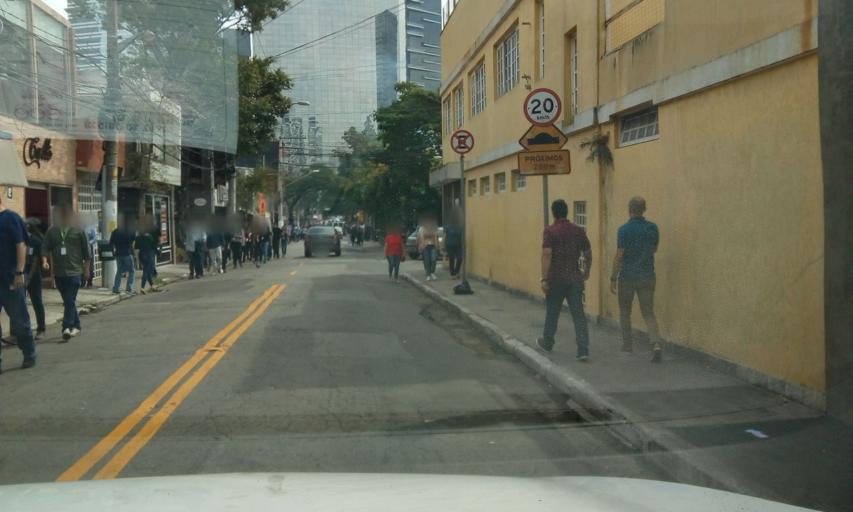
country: BR
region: Sao Paulo
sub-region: Taboao Da Serra
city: Taboao da Serra
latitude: -23.6258
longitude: -46.6986
